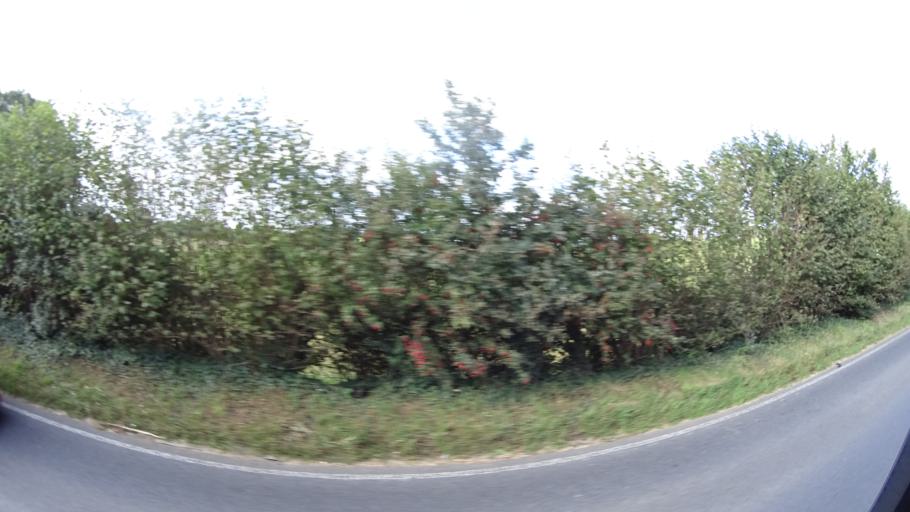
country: GB
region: England
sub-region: Dorset
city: Lytchett Matravers
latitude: 50.7681
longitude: -2.0641
